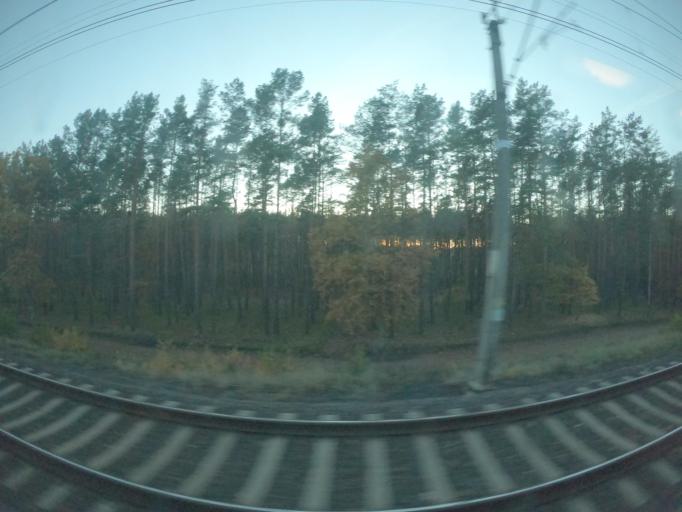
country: PL
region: West Pomeranian Voivodeship
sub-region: Powiat mysliborski
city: Boleszkowice
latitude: 52.7100
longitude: 14.5388
